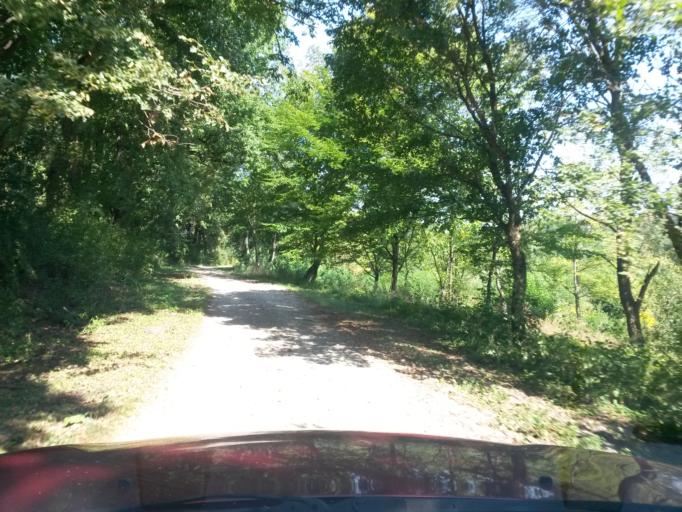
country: HU
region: Borsod-Abauj-Zemplen
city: Gonc
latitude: 48.5203
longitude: 21.2042
